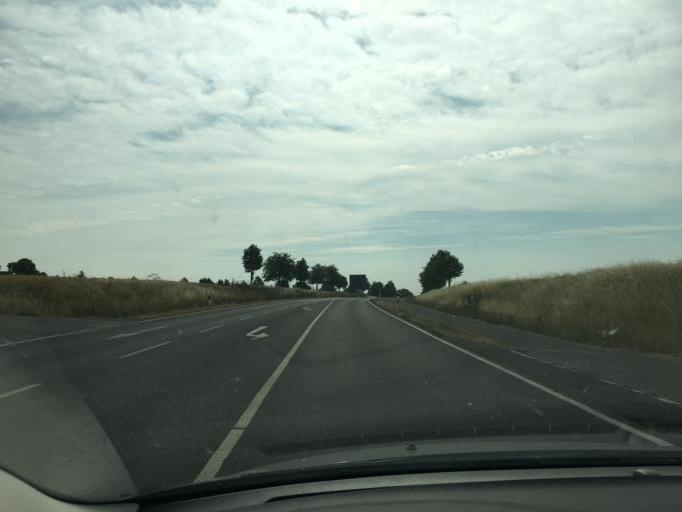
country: DE
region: Saxony-Anhalt
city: Wolmirstedt
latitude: 52.2525
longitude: 11.6066
